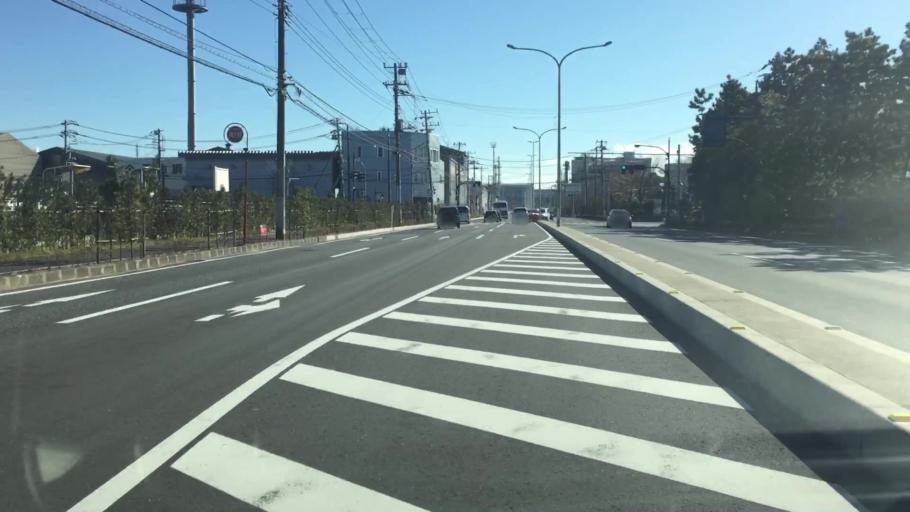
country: JP
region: Tokyo
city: Urayasu
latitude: 35.6328
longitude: 139.8901
